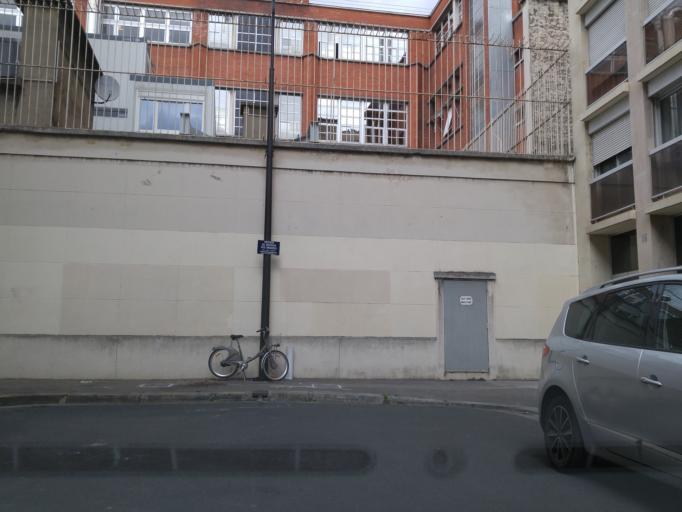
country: FR
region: Ile-de-France
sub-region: Departement des Hauts-de-Seine
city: Vanves
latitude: 48.8530
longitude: 2.2920
